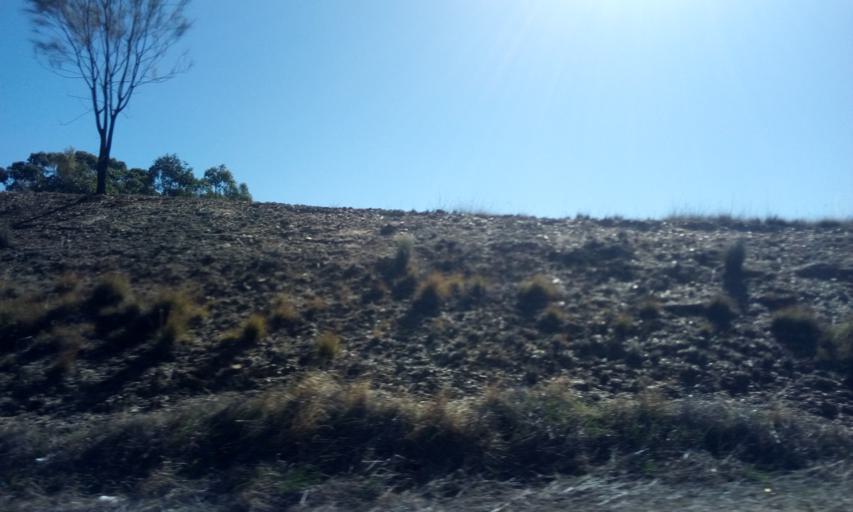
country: AU
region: New South Wales
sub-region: Yass Valley
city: Gundaroo
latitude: -35.1153
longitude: 149.3561
